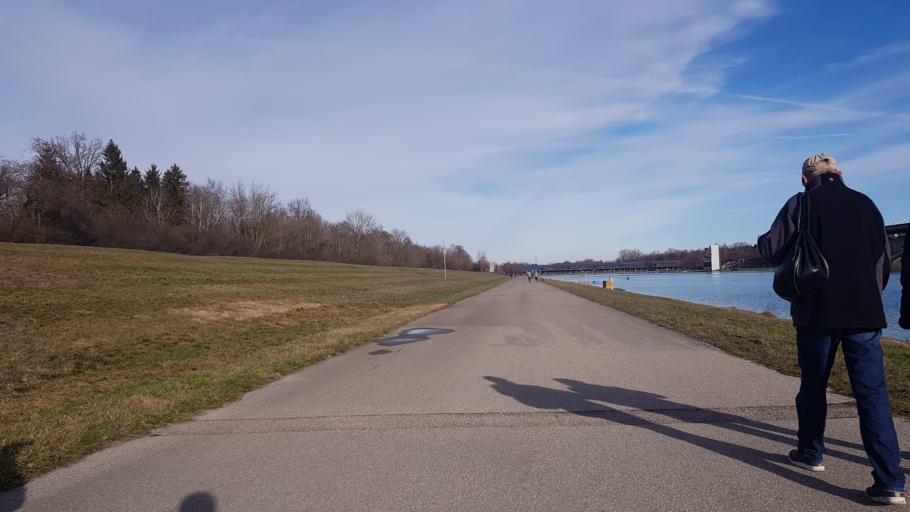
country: DE
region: Bavaria
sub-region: Upper Bavaria
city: Oberschleissheim
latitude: 48.2454
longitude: 11.5173
